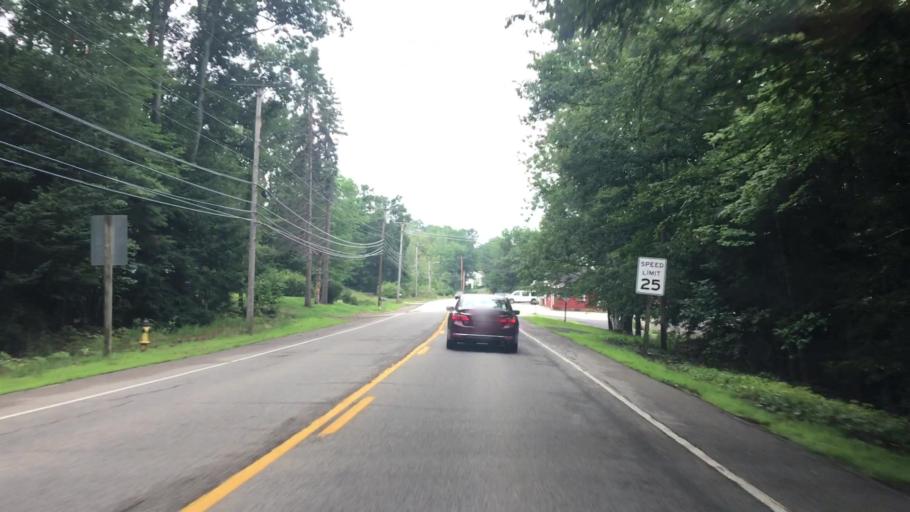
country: US
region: Maine
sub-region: York County
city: Sanford (historical)
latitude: 43.4528
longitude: -70.7665
